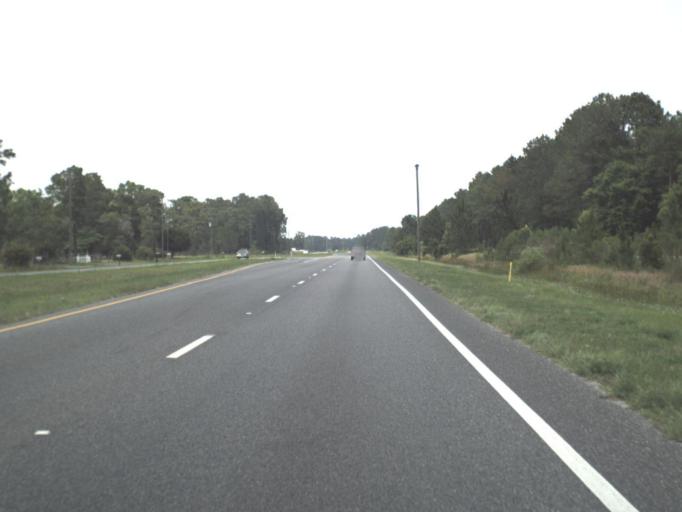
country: US
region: Florida
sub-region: Putnam County
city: Palatka
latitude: 29.7351
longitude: -81.6470
